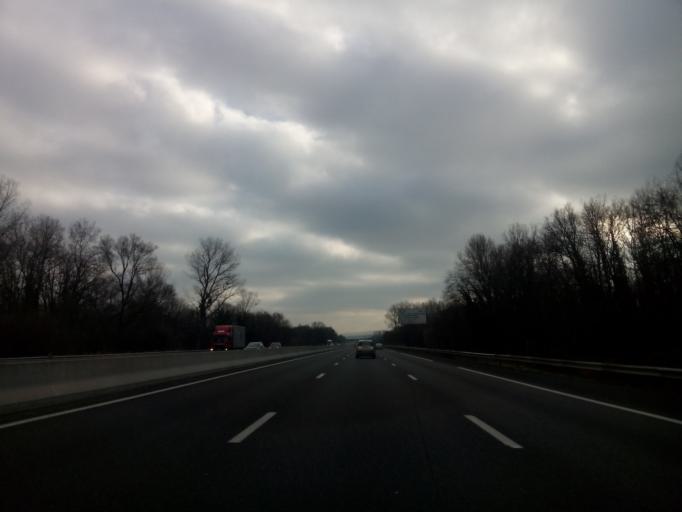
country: FR
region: Rhone-Alpes
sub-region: Departement de l'Isere
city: La Verpilliere
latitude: 45.6391
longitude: 5.1501
